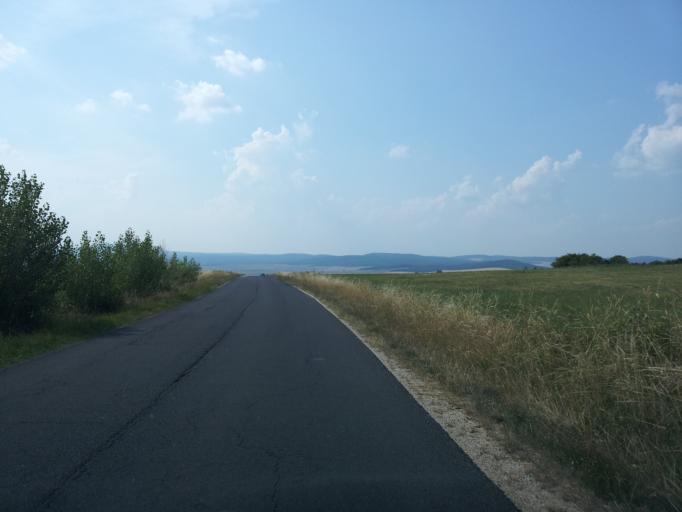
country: HU
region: Veszprem
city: Balatonfured
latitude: 46.9973
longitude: 17.8010
